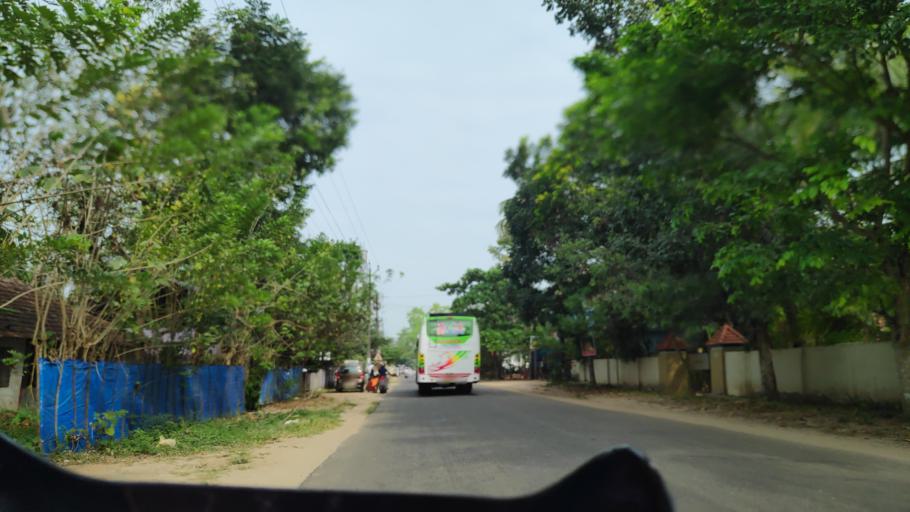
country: IN
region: Kerala
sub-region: Alappuzha
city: Kutiatodu
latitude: 9.8148
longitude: 76.3516
